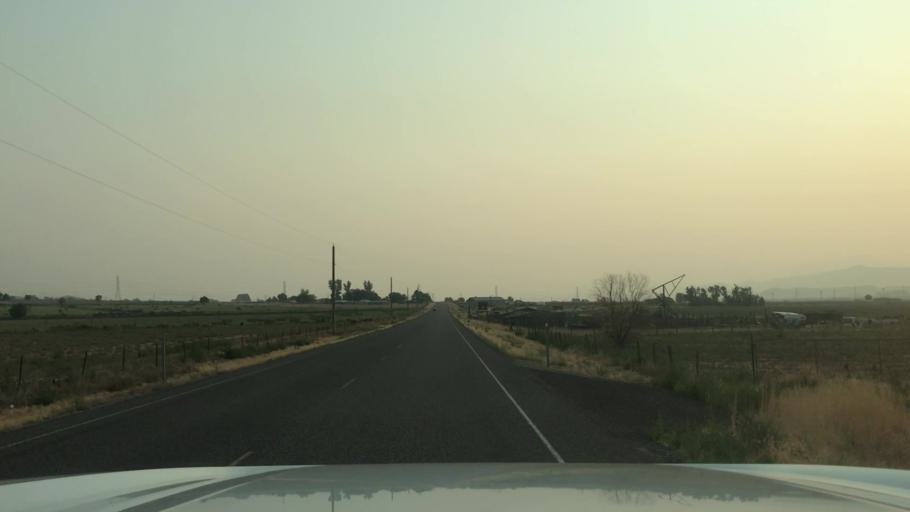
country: US
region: Utah
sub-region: Sevier County
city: Aurora
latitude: 38.8838
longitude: -111.9595
